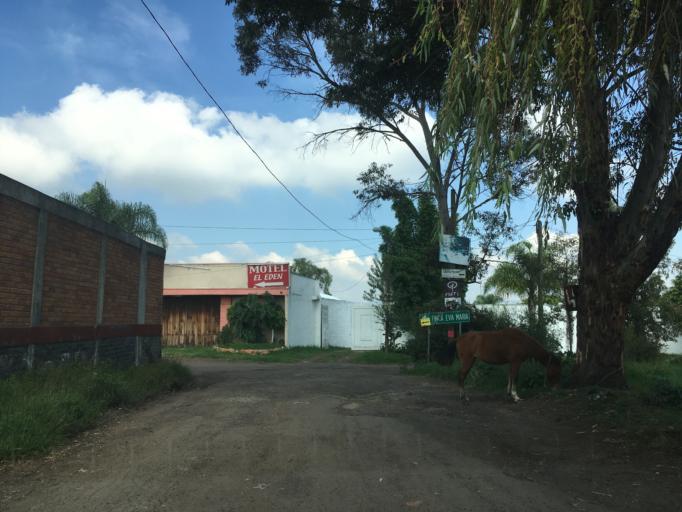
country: MX
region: Michoacan
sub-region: Morelia
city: Morelos
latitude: 19.6466
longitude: -101.2507
